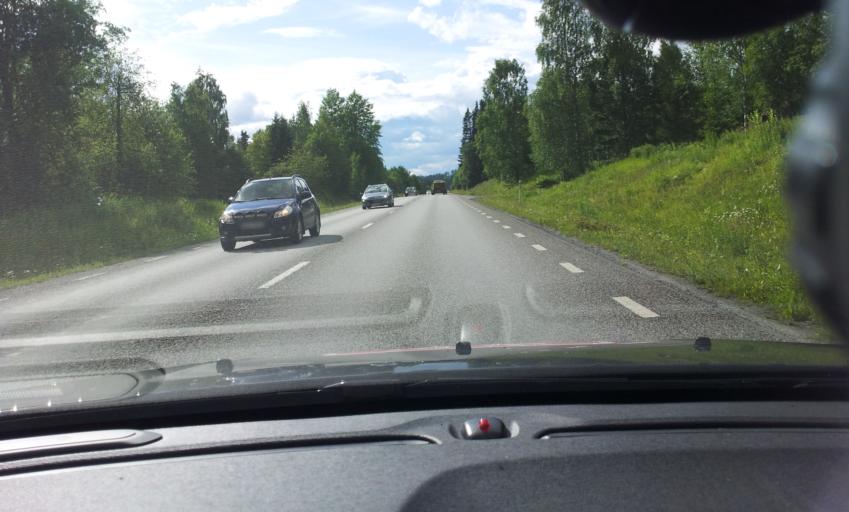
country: SE
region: Jaemtland
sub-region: Are Kommun
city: Jarpen
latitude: 63.3106
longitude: 13.6716
